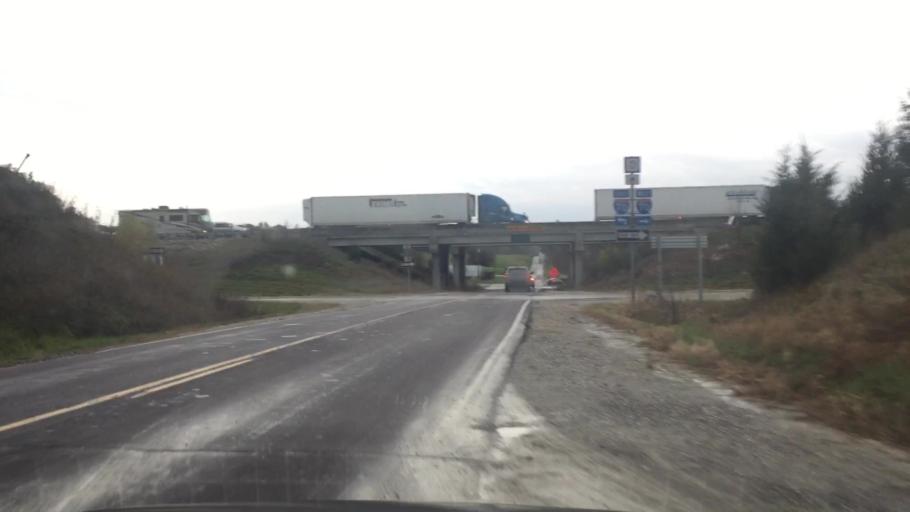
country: US
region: Missouri
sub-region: Boone County
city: Columbia
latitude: 38.9745
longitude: -92.4956
